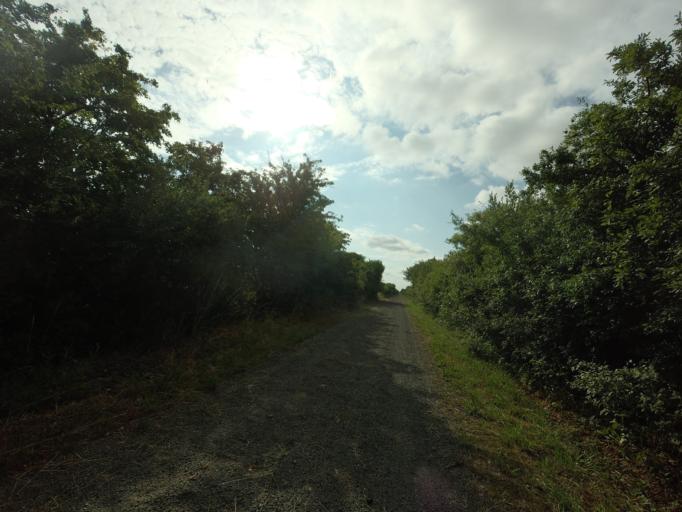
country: SE
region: Skane
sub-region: Helsingborg
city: Odakra
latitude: 56.1652
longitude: 12.7336
